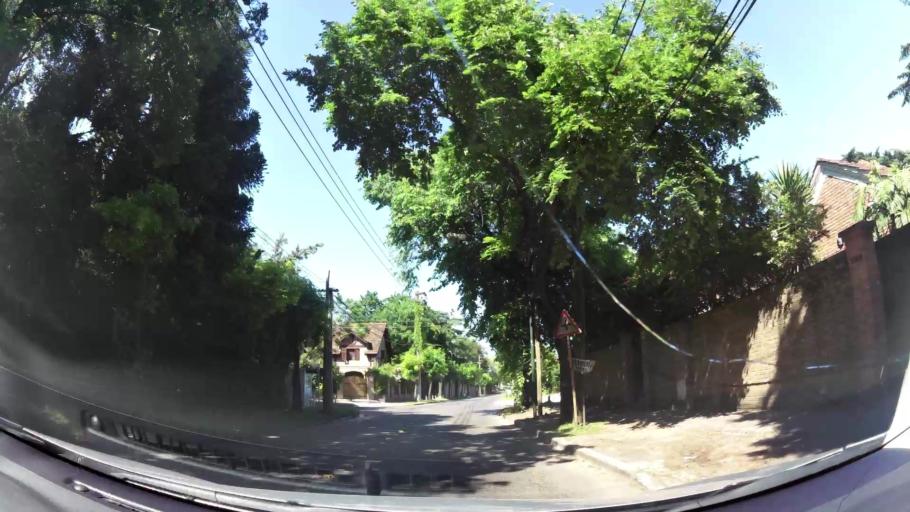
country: AR
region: Buenos Aires
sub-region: Partido de Tigre
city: Tigre
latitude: -34.4933
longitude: -58.5725
